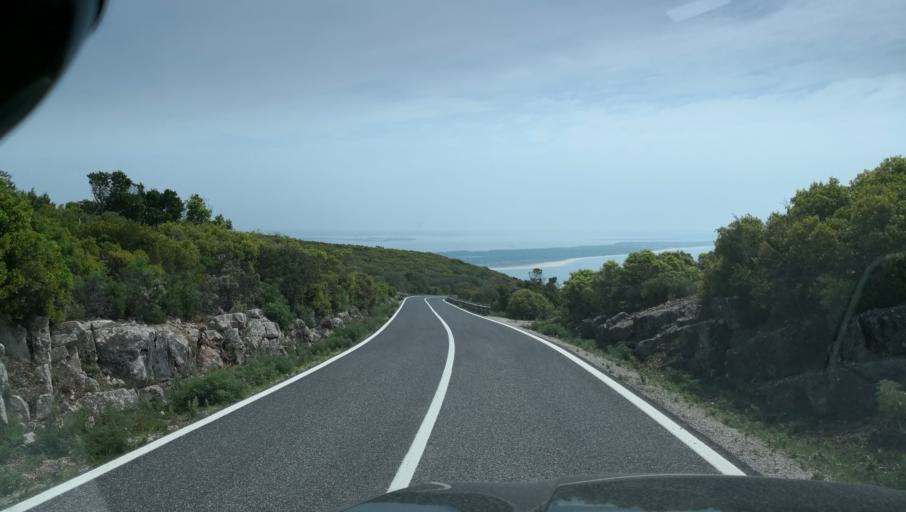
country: PT
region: Setubal
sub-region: Setubal
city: Setubal
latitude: 38.4888
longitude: -8.9484
